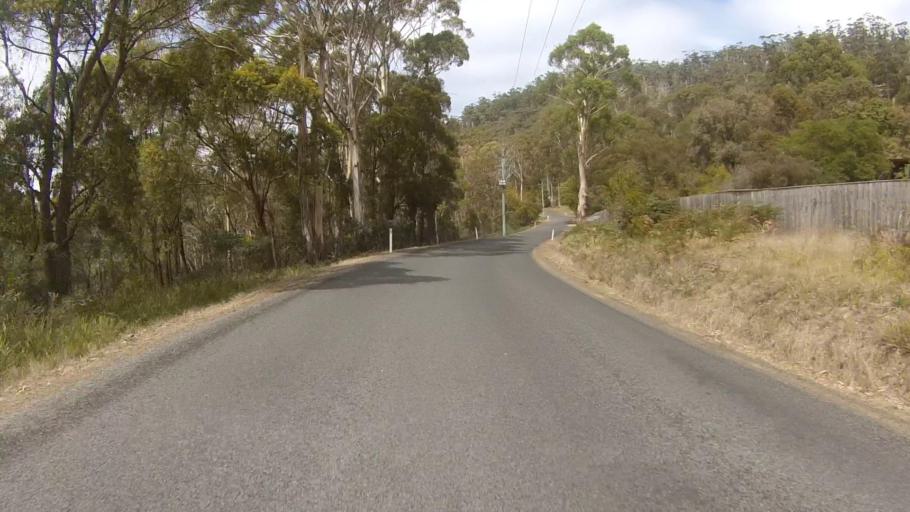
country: AU
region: Tasmania
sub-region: Kingborough
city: Blackmans Bay
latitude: -43.0234
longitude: 147.3234
